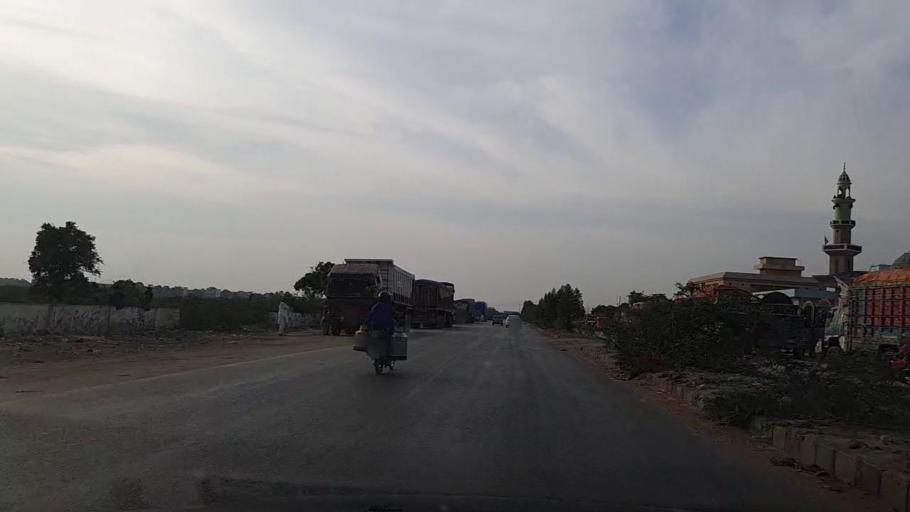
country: PK
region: Sindh
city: Gharo
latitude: 24.8496
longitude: 67.4259
